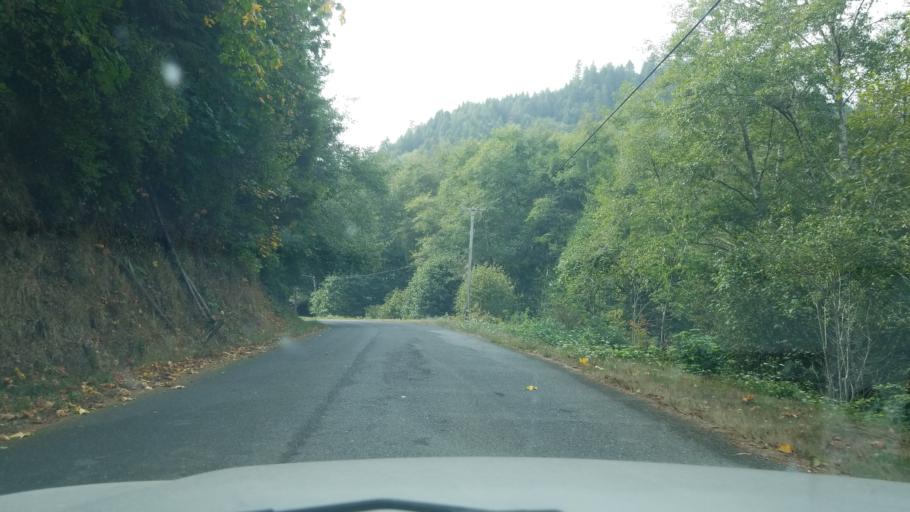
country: US
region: California
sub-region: Del Norte County
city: Bertsch-Oceanview
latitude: 41.5123
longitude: -124.0332
